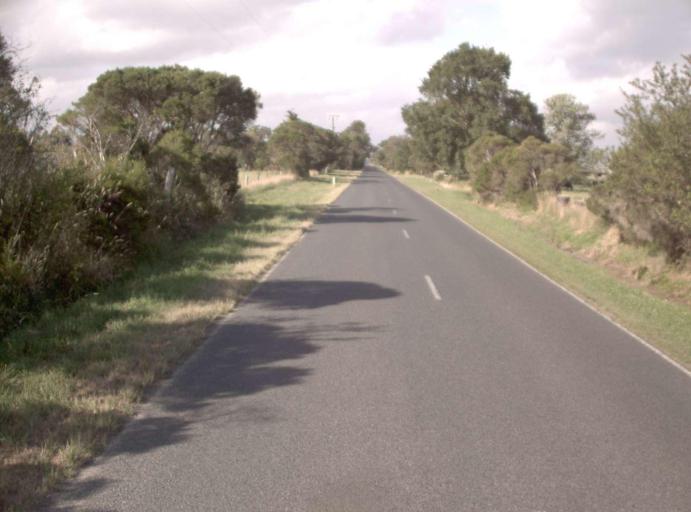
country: AU
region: Victoria
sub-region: Cardinia
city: Bunyip
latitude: -38.1789
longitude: 145.7149
